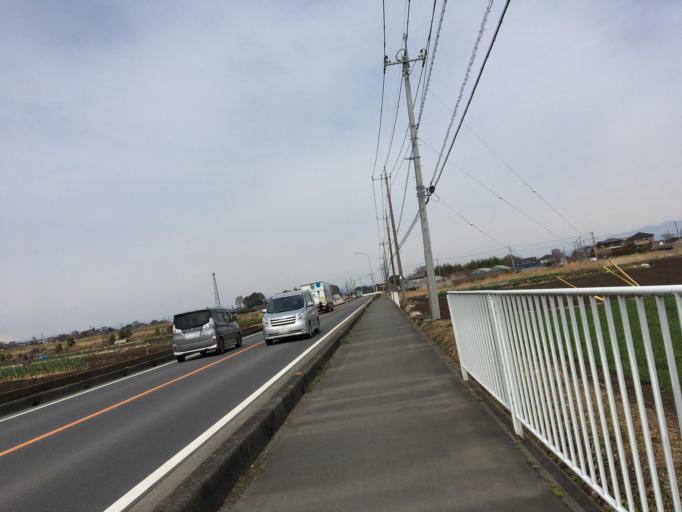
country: JP
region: Saitama
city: Yorii
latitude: 36.1407
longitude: 139.2116
